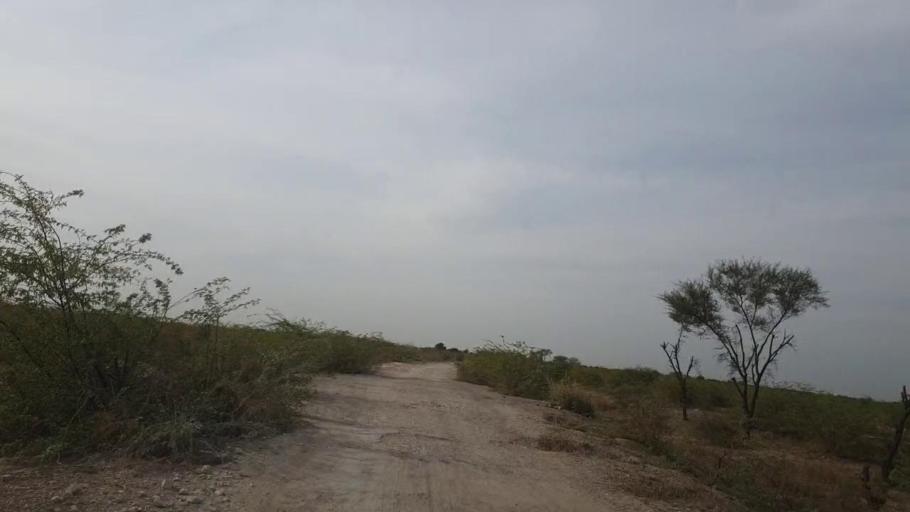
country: PK
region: Sindh
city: Nabisar
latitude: 24.9975
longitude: 69.5448
